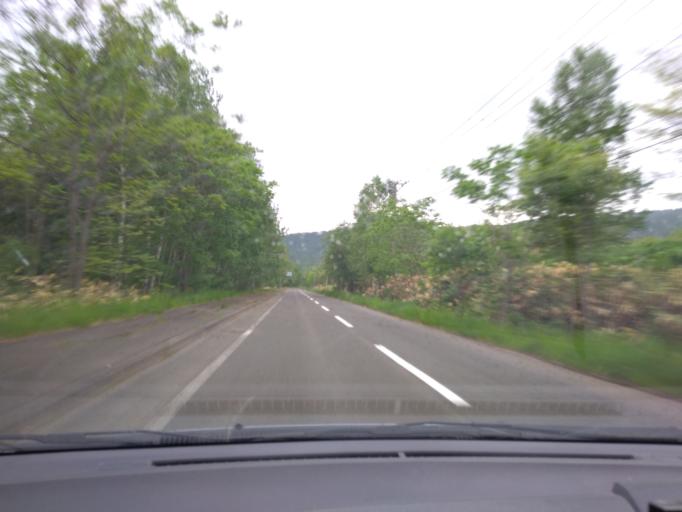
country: JP
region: Hokkaido
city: Shimo-furano
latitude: 43.1766
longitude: 142.5340
